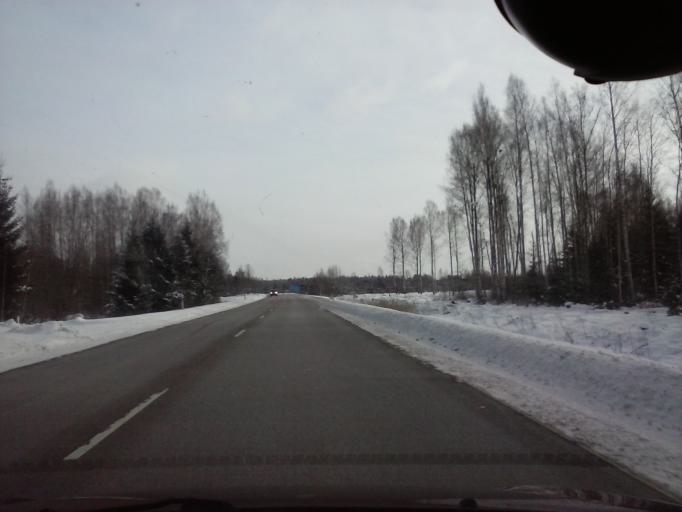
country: EE
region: Paernumaa
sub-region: Saarde vald
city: Kilingi-Nomme
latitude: 58.1731
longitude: 24.8095
